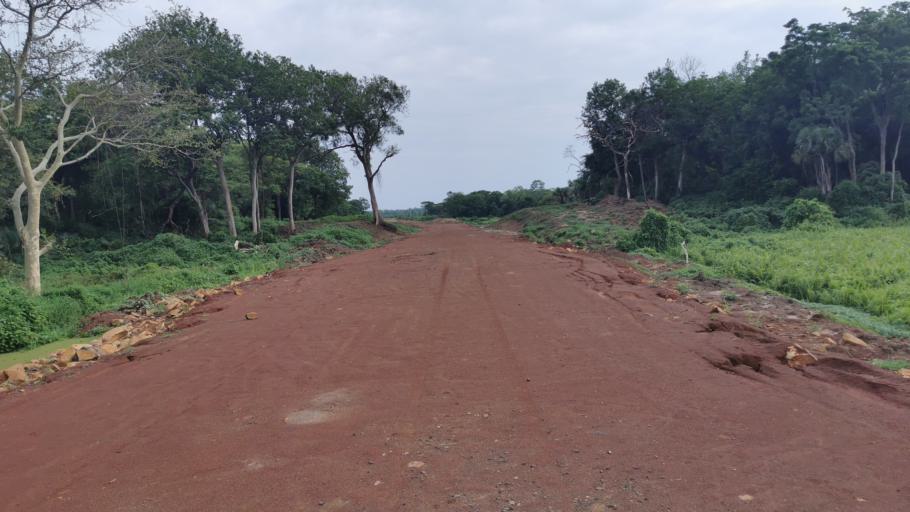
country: ET
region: Gambela
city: Gambela
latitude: 7.8694
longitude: 34.4945
